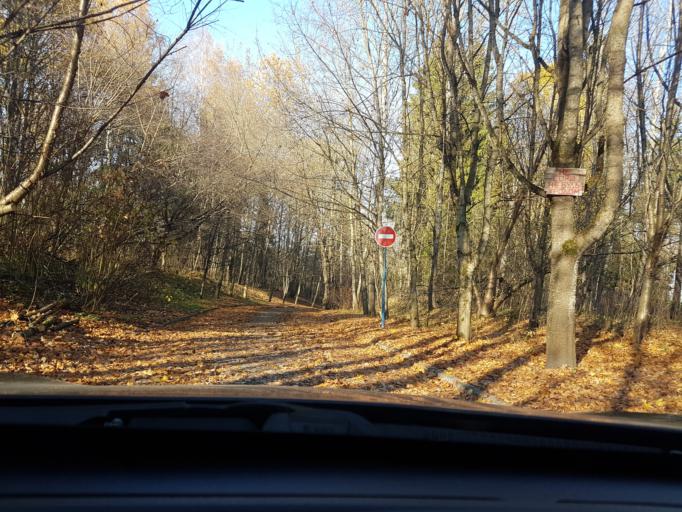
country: BY
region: Minsk
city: Azyartso
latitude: 53.8094
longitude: 27.3829
